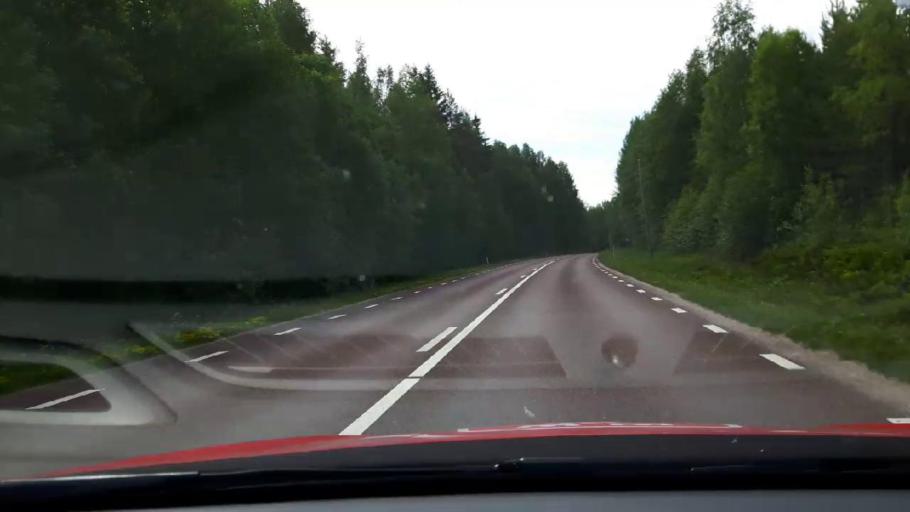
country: SE
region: Jaemtland
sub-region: Harjedalens Kommun
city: Sveg
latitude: 62.0720
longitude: 14.9394
